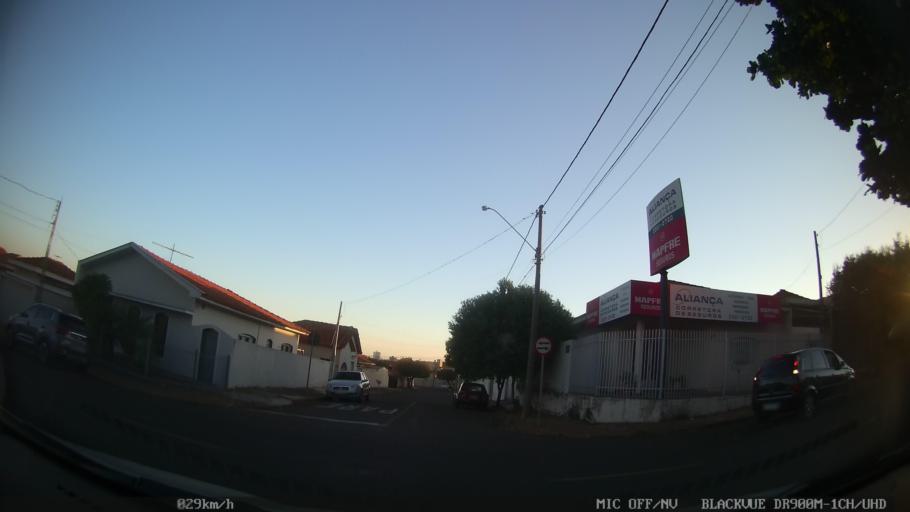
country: BR
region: Sao Paulo
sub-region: Sao Jose Do Rio Preto
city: Sao Jose do Rio Preto
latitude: -20.8036
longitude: -49.3685
